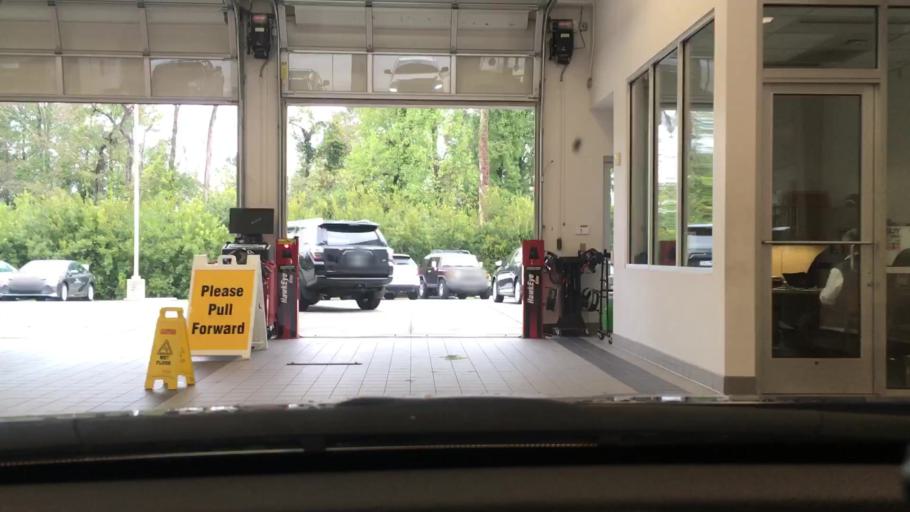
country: US
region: South Carolina
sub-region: Lexington County
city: West Columbia
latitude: 34.0002
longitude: -81.0990
